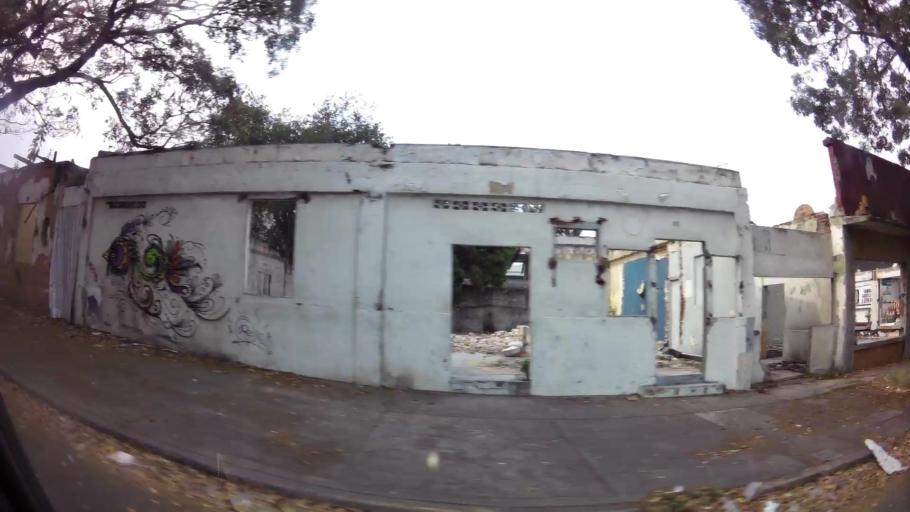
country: HN
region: Cortes
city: San Pedro Sula
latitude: 15.5025
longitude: -88.0370
